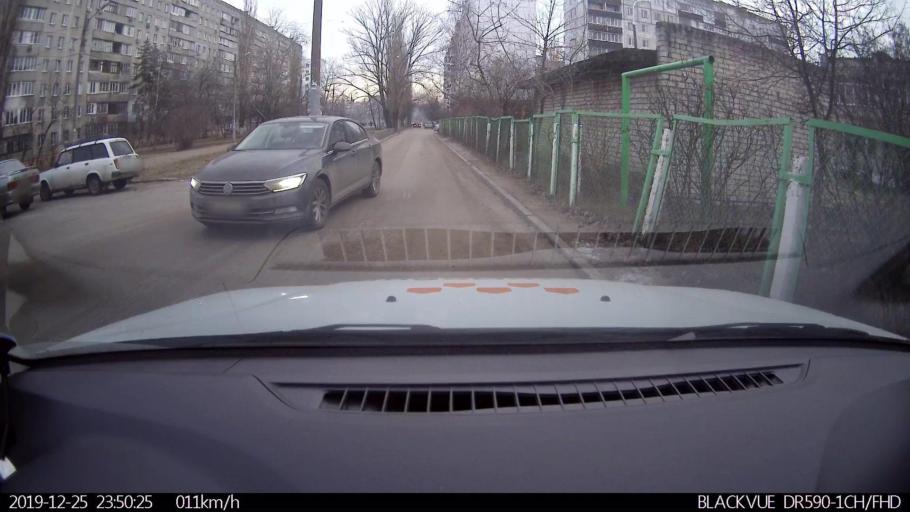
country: RU
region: Nizjnij Novgorod
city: Nizhniy Novgorod
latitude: 56.3327
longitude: 43.9436
